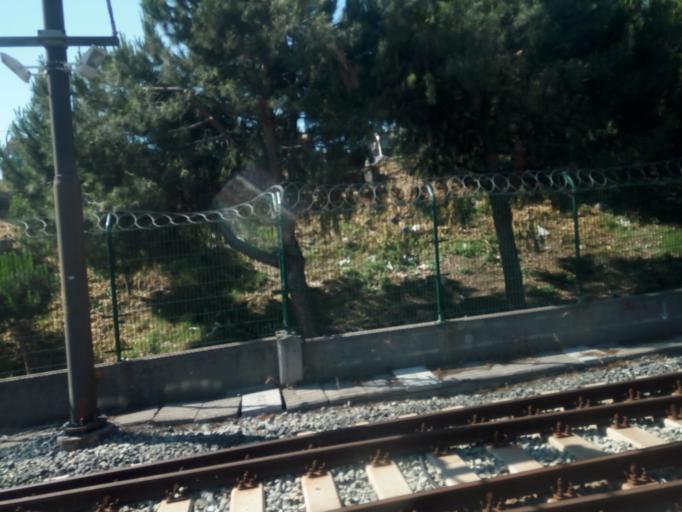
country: TR
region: Istanbul
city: Bahcelievler
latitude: 40.9904
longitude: 28.8386
